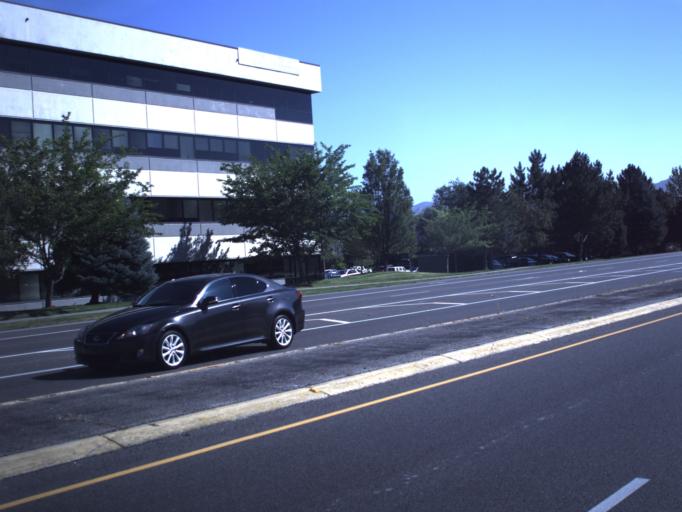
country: US
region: Utah
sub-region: Salt Lake County
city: Centerfield
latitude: 40.6743
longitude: -111.9137
